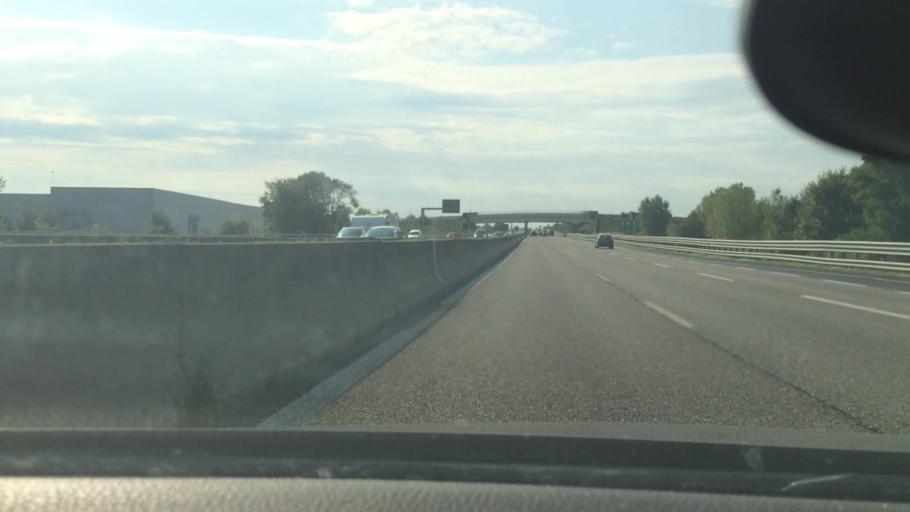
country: IT
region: Emilia-Romagna
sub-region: Provincia di Piacenza
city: Piacenza
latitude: 45.0414
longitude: 9.7582
